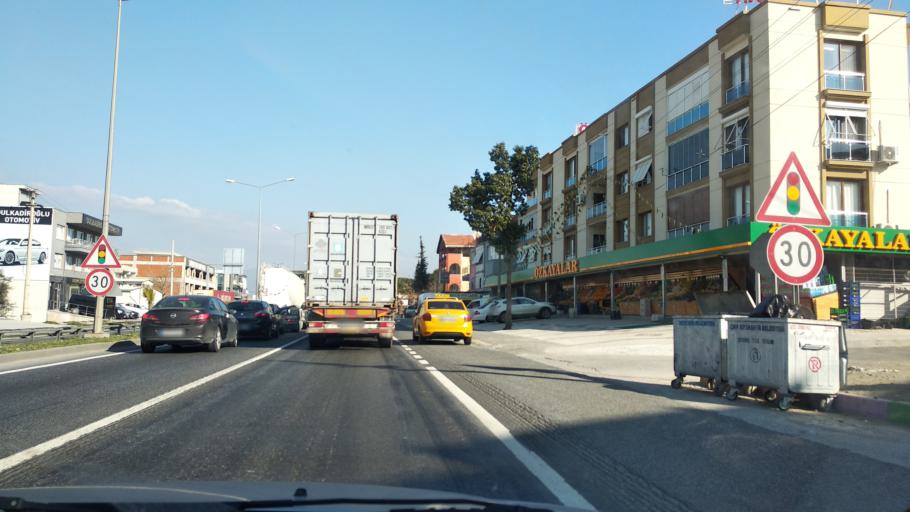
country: TR
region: Izmir
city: Menemen
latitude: 38.5754
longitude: 27.0620
